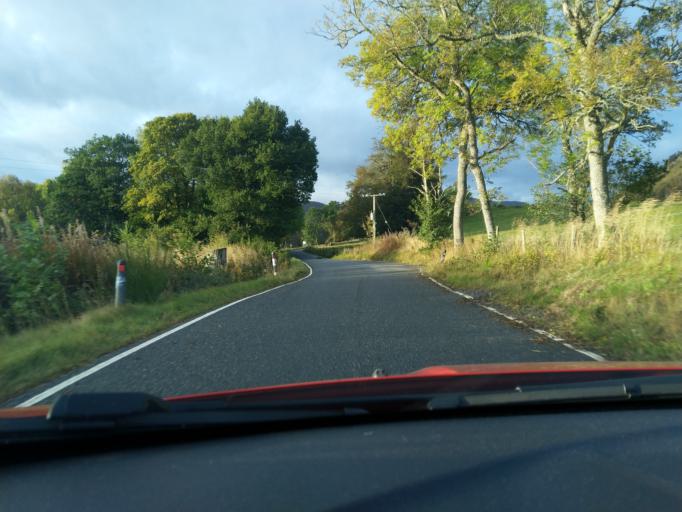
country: GB
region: Scotland
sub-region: Perth and Kinross
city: Aberfeldy
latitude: 56.7052
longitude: -4.1248
